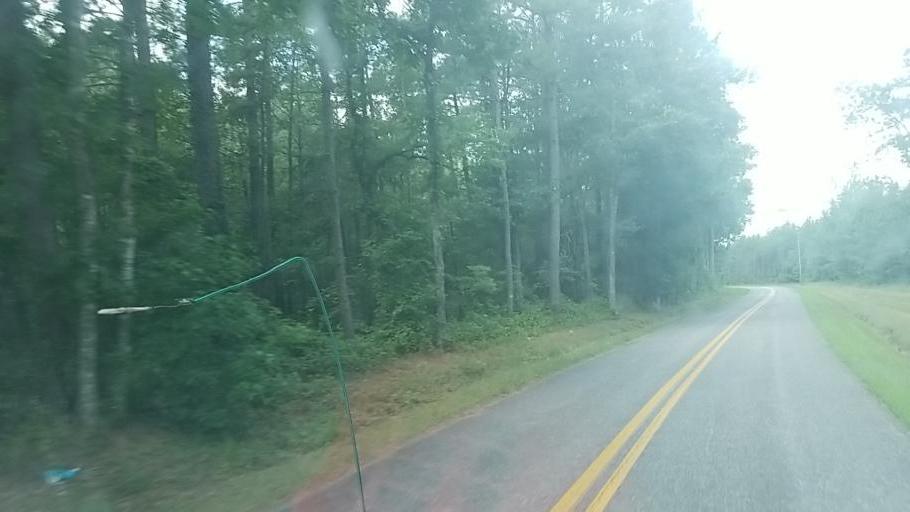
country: US
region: Maryland
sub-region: Worcester County
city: Snow Hill
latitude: 38.2565
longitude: -75.4450
